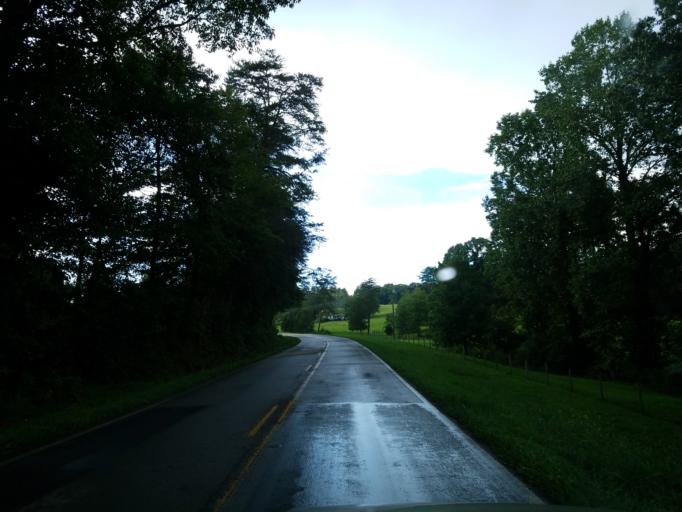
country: US
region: Georgia
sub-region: White County
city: Cleveland
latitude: 34.6106
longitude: -83.8642
